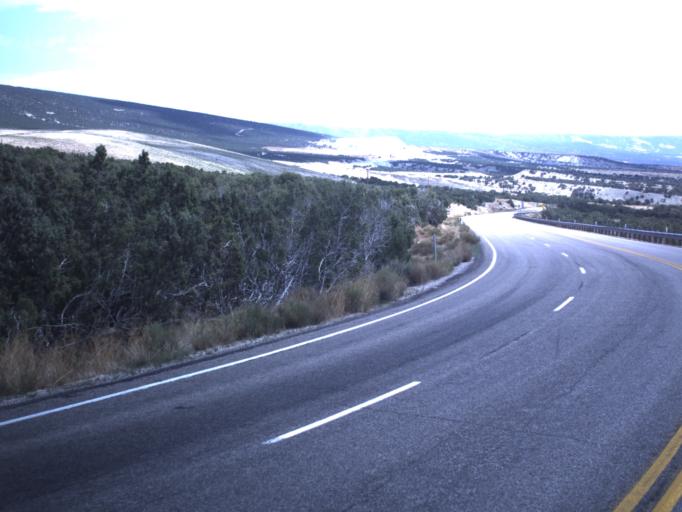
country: US
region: Utah
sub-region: Uintah County
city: Vernal
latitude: 40.6087
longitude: -109.4775
